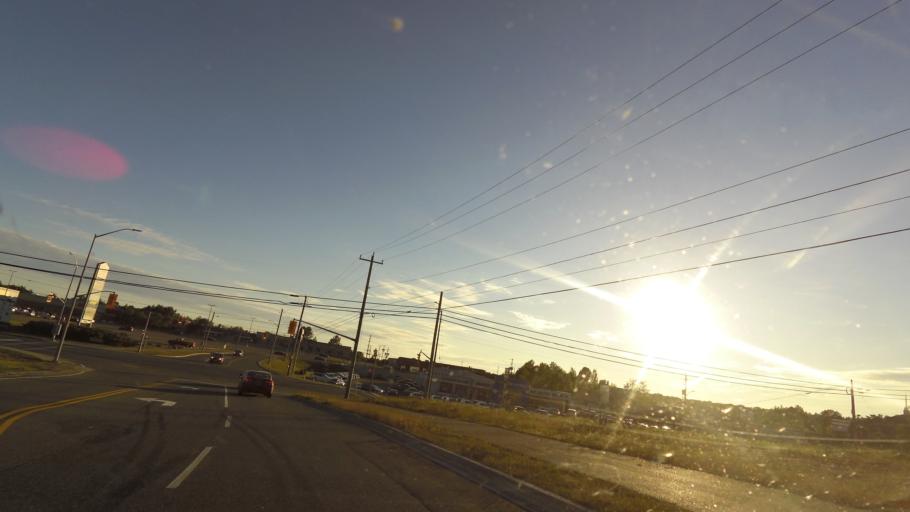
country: CA
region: Ontario
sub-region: Parry Sound District
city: Parry Sound
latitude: 45.3609
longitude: -80.0398
